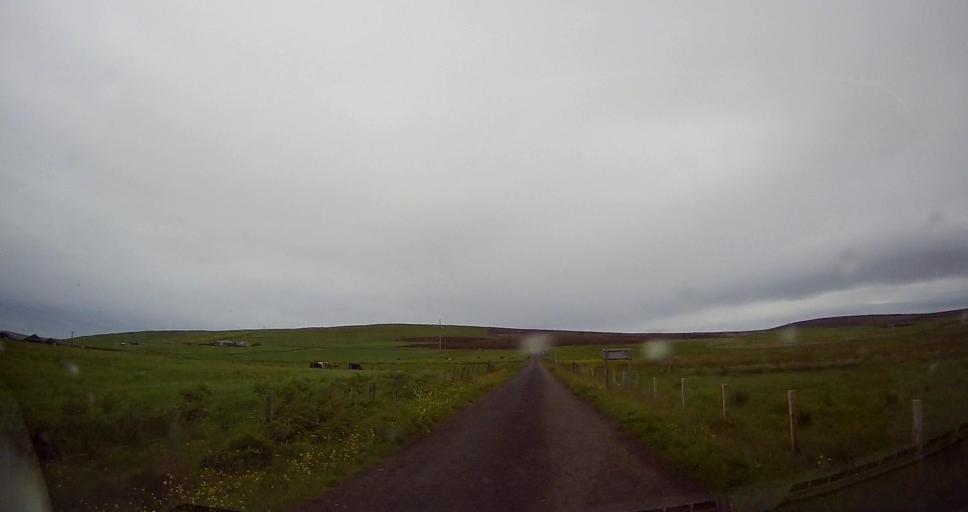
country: GB
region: Scotland
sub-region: Orkney Islands
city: Stromness
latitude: 59.0878
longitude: -3.1830
